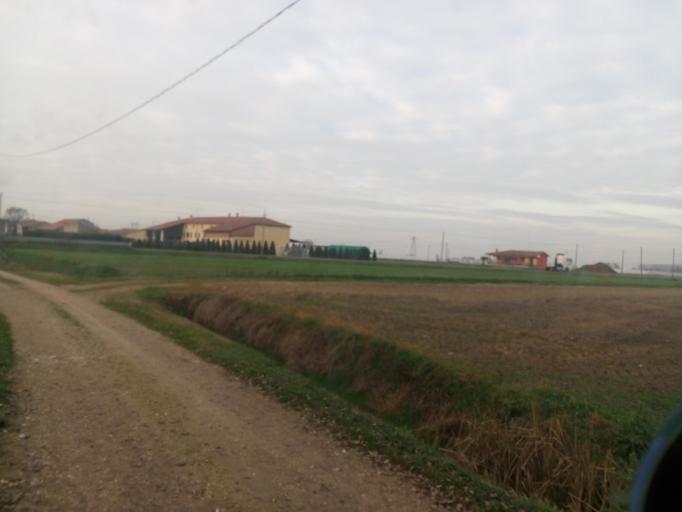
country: IT
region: Veneto
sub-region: Provincia di Verona
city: Trevenzuolo
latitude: 45.2953
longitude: 10.9159
